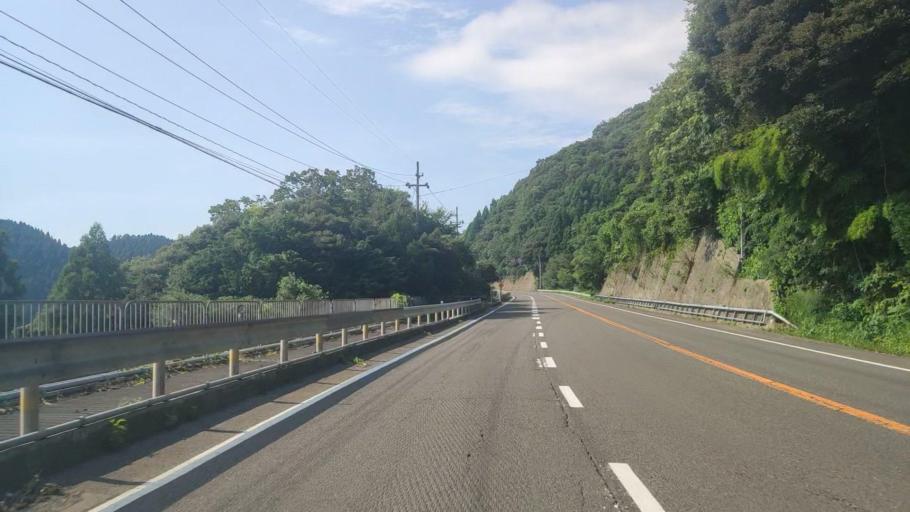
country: JP
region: Fukui
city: Tsuruga
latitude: 35.7582
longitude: 136.1050
